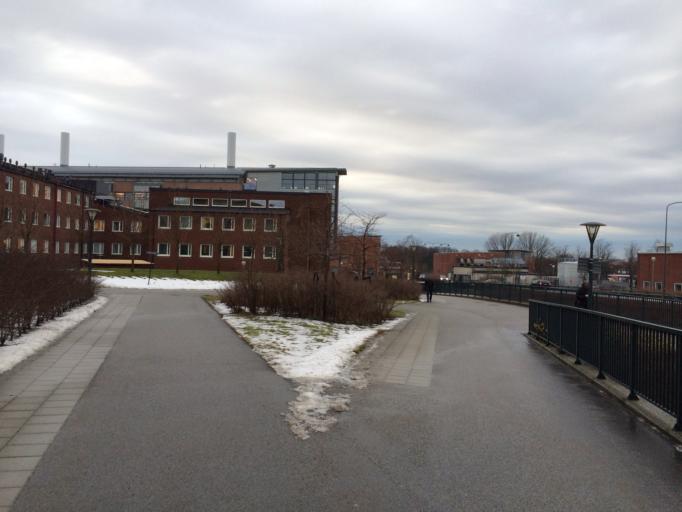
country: SE
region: Skane
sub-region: Lunds Kommun
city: Lund
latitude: 55.7129
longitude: 13.2043
